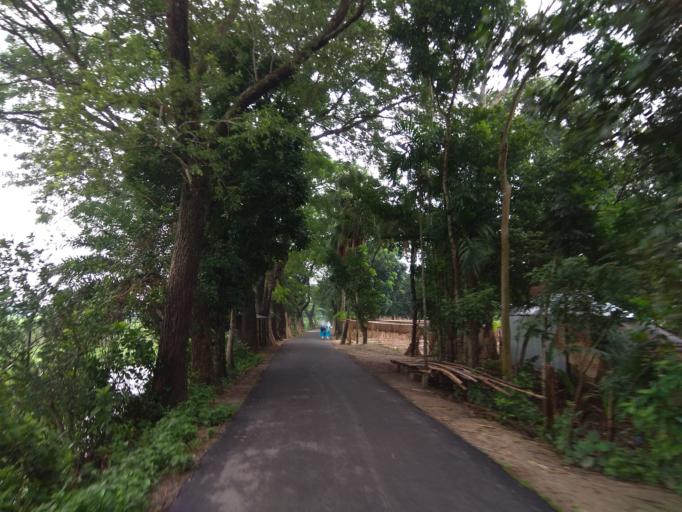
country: BD
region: Dhaka
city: Dohar
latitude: 23.4747
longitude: 90.0599
